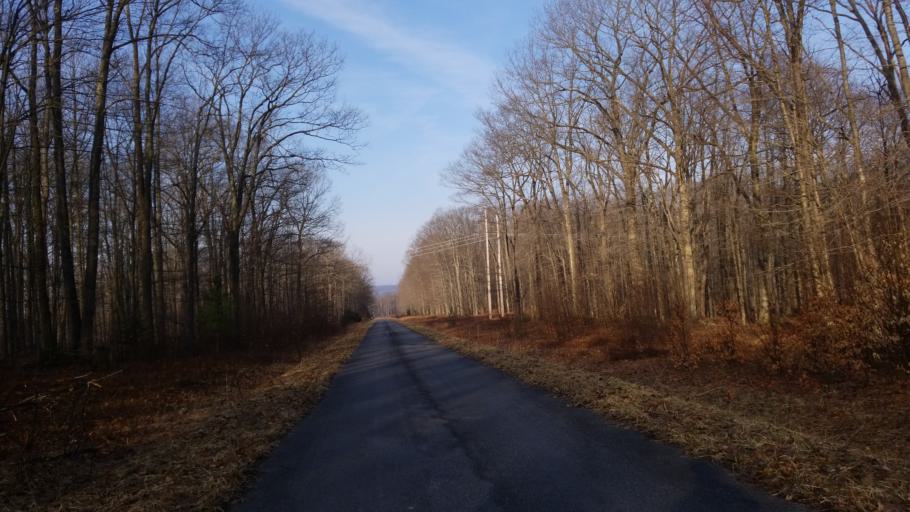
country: US
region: Pennsylvania
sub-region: Clearfield County
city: Shiloh
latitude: 41.2255
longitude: -78.2257
